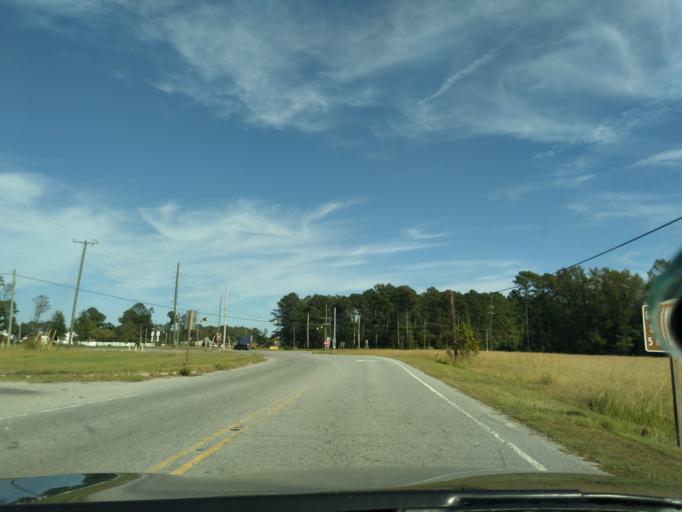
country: US
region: North Carolina
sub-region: Beaufort County
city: River Road
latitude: 35.5281
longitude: -76.9501
